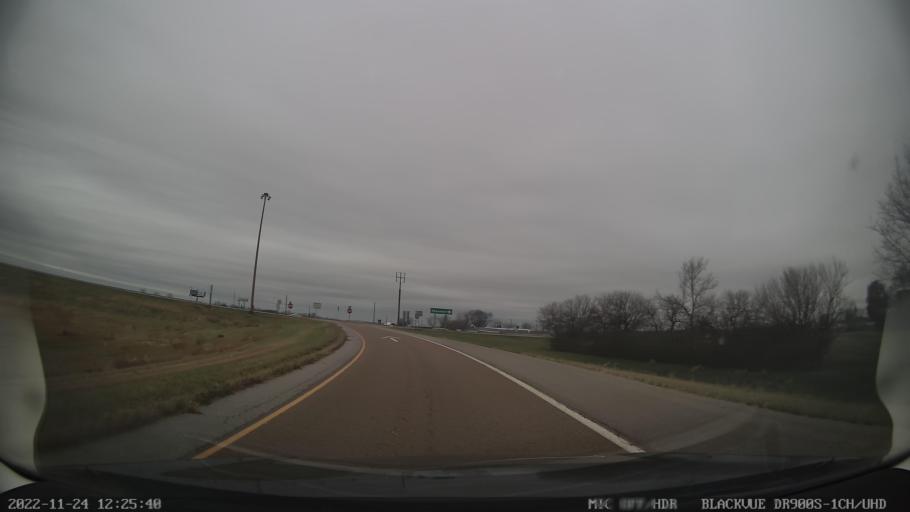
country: US
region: Illinois
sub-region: Macoupin County
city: Staunton
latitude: 39.0221
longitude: -89.7519
